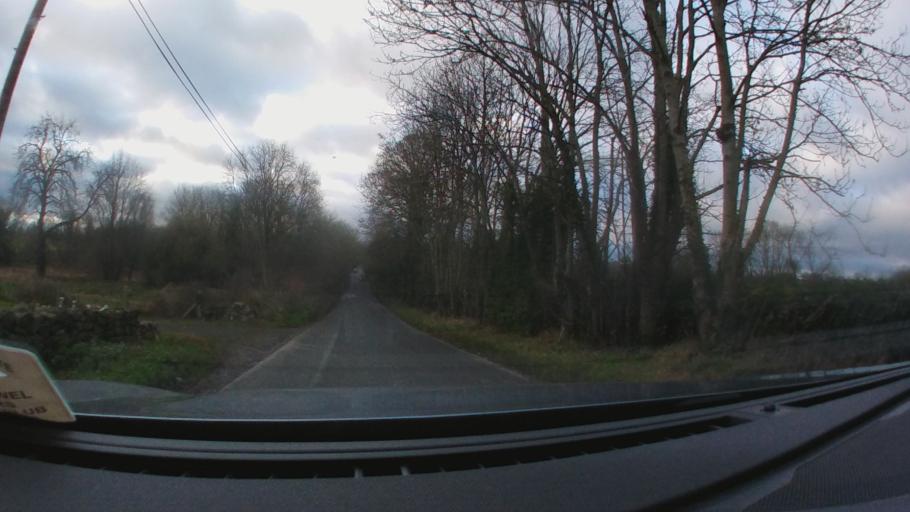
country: IE
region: Leinster
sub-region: Kilkenny
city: Thomastown
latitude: 52.5552
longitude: -7.1206
